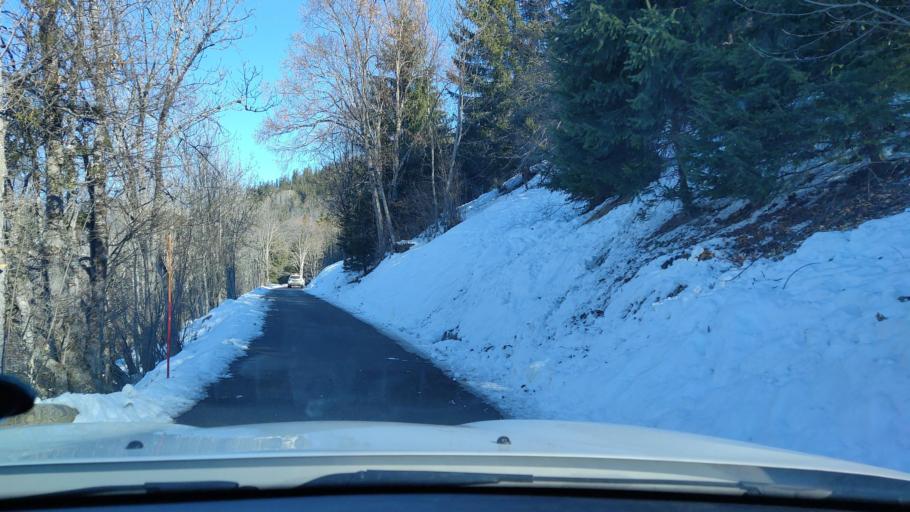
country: FR
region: Rhone-Alpes
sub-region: Departement de la Savoie
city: Les Allues
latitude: 45.4285
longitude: 6.5646
